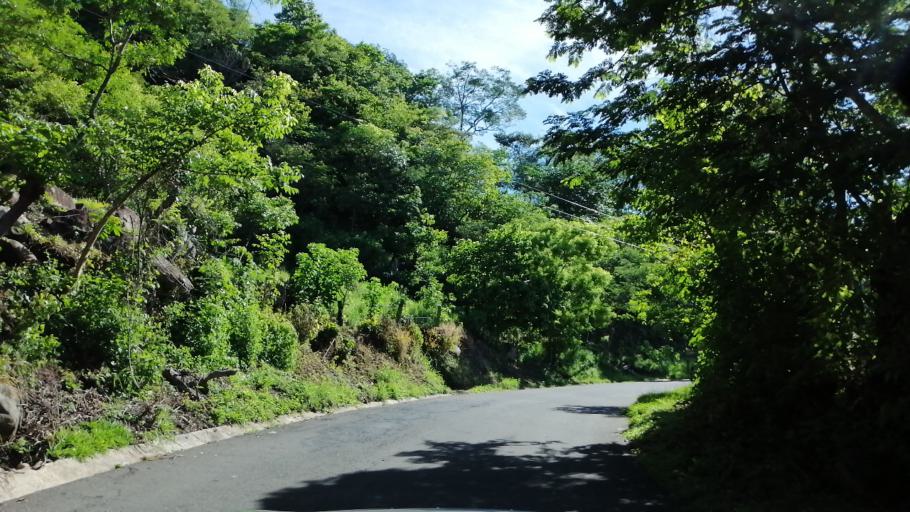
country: SV
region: Morazan
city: Corinto
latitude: 13.7987
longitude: -88.0044
